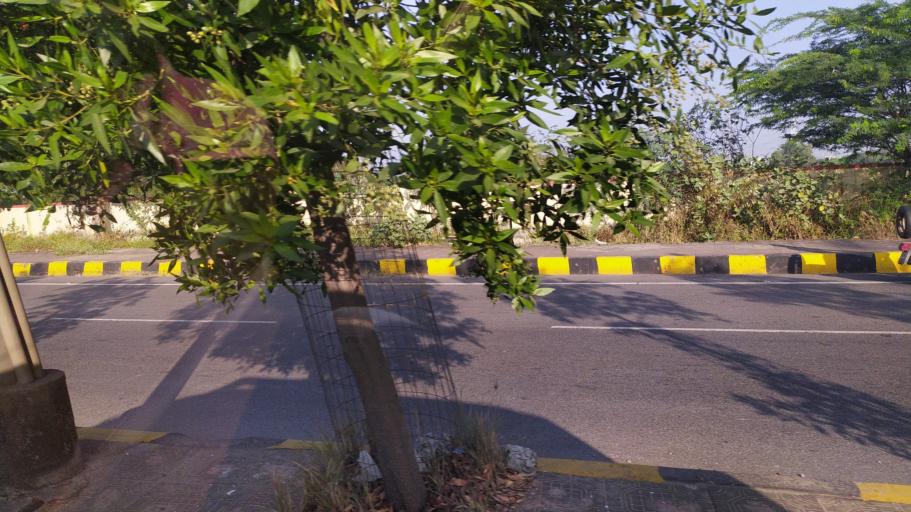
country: IN
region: Telangana
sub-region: Hyderabad
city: Hyderabad
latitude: 17.3228
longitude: 78.4045
